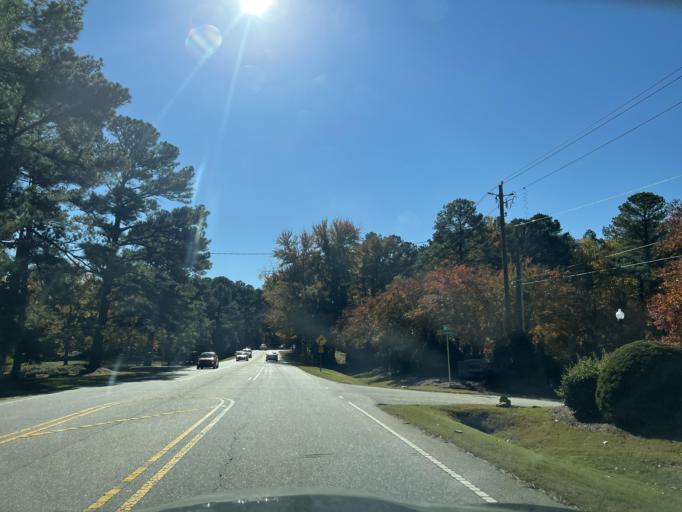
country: US
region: North Carolina
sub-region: Wake County
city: Garner
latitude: 35.7025
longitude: -78.6891
